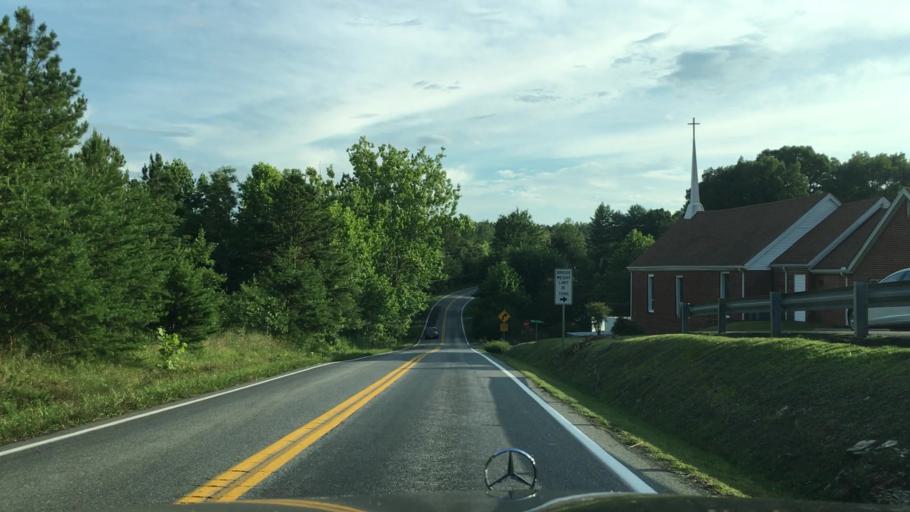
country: US
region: Virginia
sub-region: Campbell County
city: Timberlake
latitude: 37.2664
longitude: -79.2641
